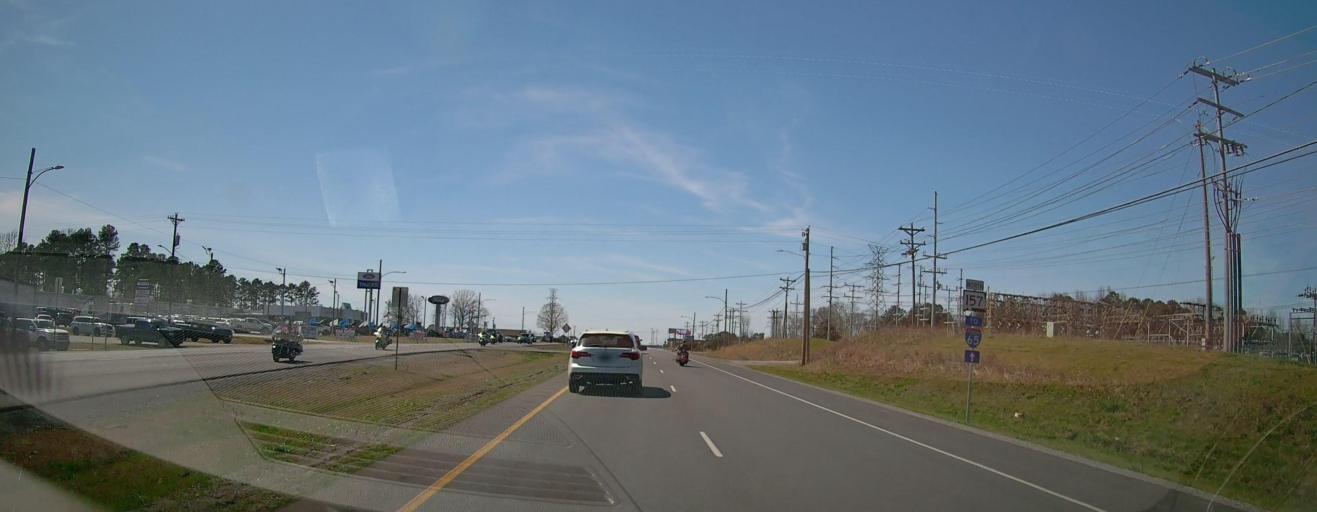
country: US
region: Alabama
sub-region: Cullman County
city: Cullman
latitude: 34.2065
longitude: -86.8602
